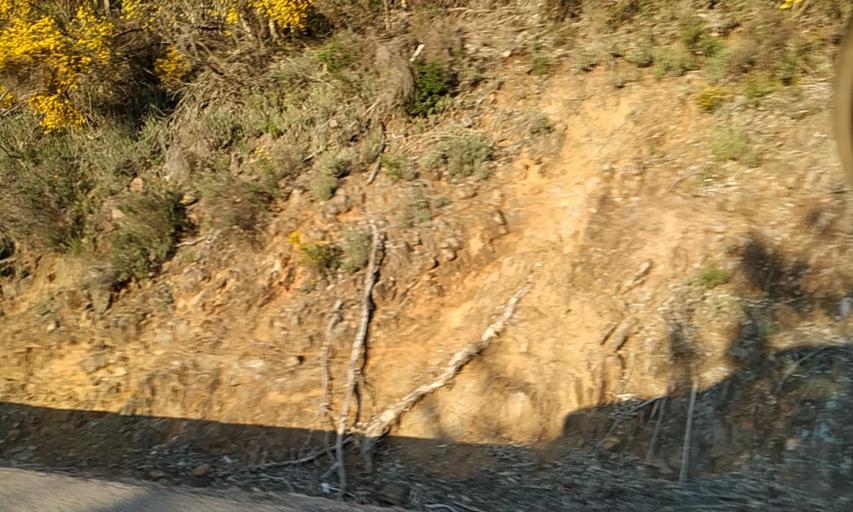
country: PT
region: Portalegre
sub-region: Portalegre
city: Sao Juliao
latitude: 39.3447
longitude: -7.2757
